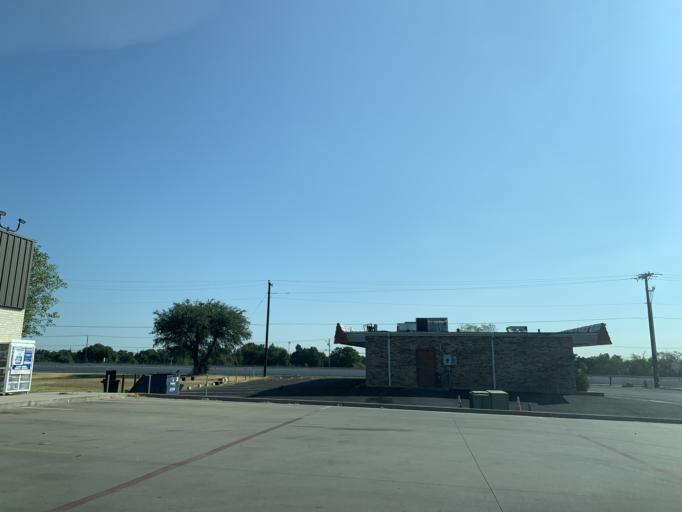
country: US
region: Texas
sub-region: Tarrant County
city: Lakeside
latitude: 32.8262
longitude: -97.4810
